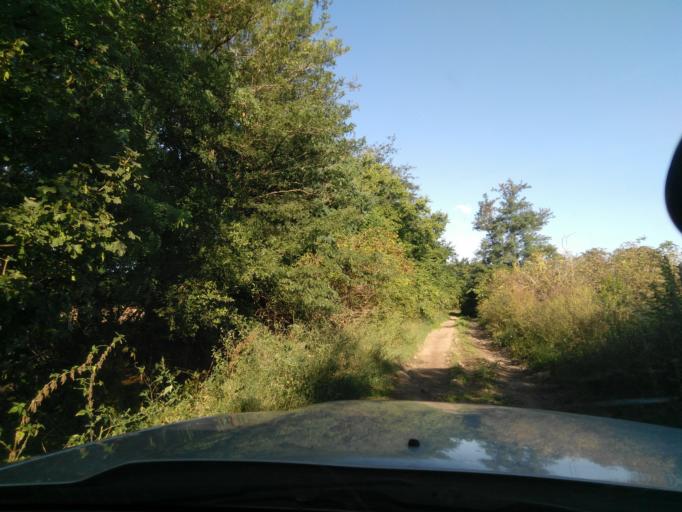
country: HU
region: Fejer
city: Kapolnasnyek
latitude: 47.2693
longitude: 18.7097
